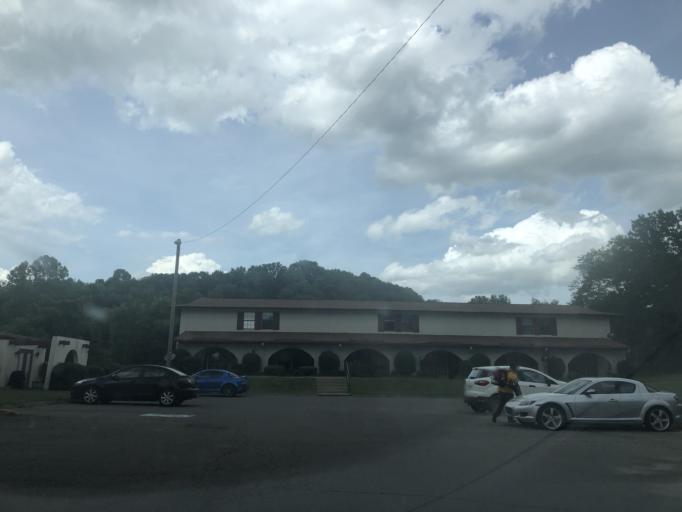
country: US
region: Tennessee
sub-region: Davidson County
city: Belle Meade
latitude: 36.0801
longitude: -86.9180
